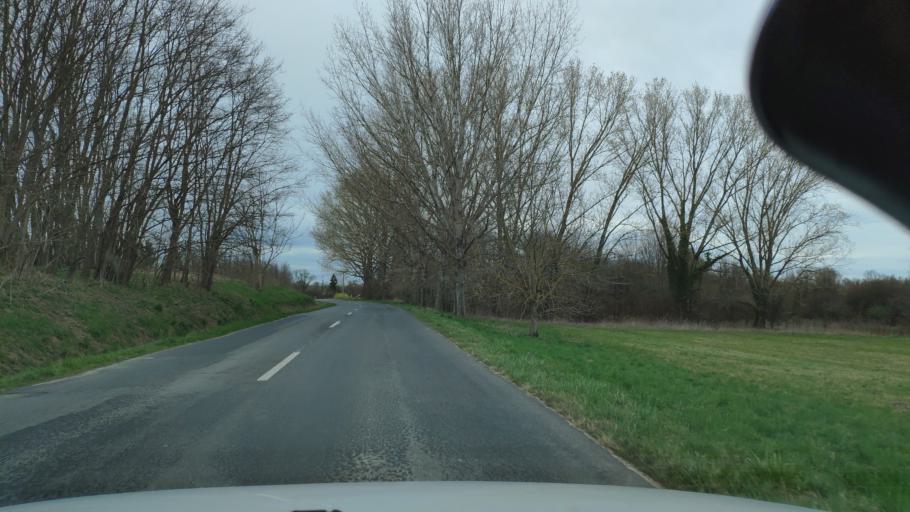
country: HU
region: Zala
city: Sarmellek
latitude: 46.6715
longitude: 17.1120
